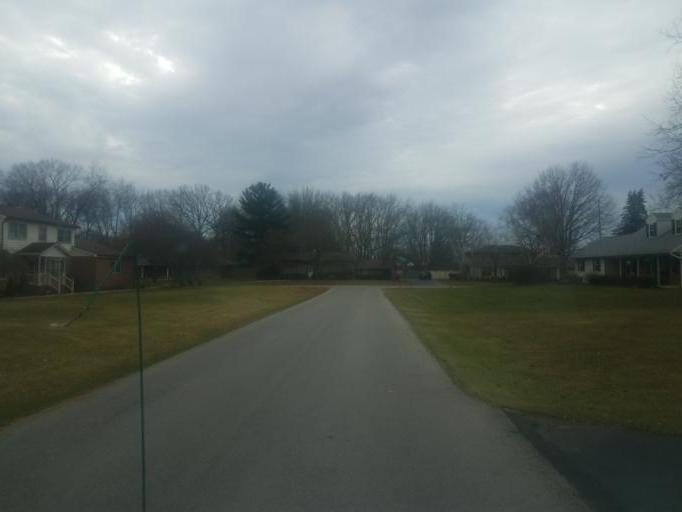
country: US
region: Ohio
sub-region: Marion County
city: Marion
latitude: 40.5653
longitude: -83.0769
